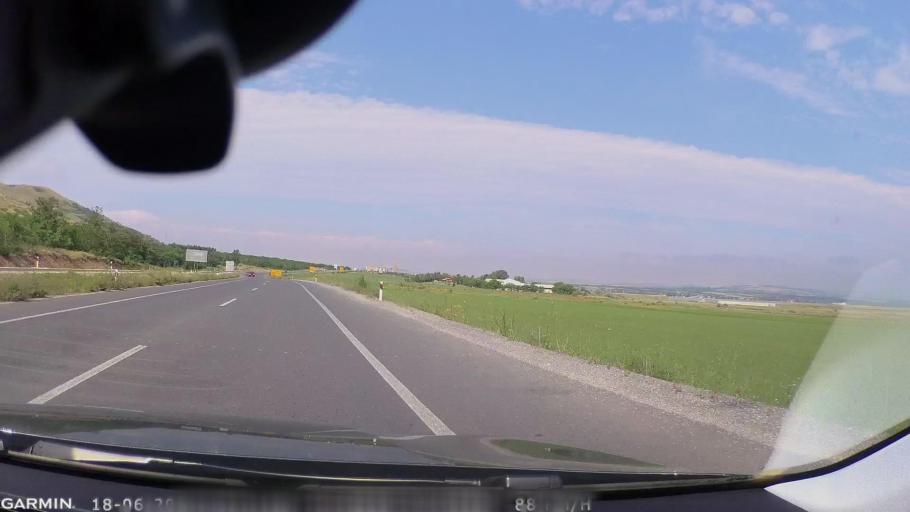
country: MK
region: Sveti Nikole
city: Sveti Nikole
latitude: 41.8279
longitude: 22.0035
